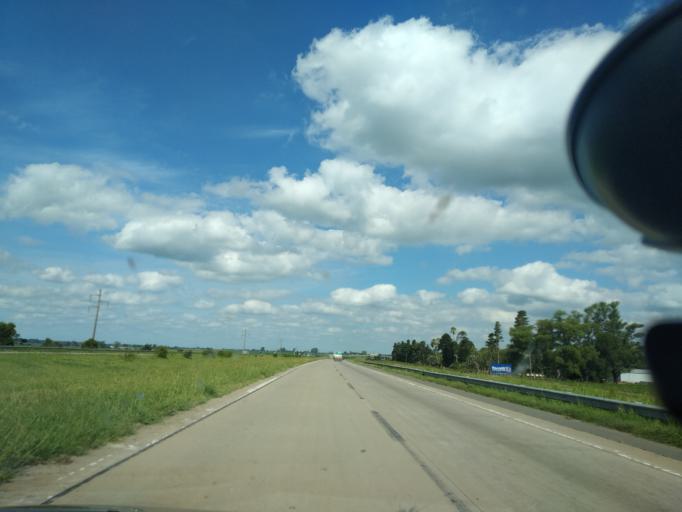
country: AR
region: Santa Fe
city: Canada de Gomez
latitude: -32.8432
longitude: -61.4114
